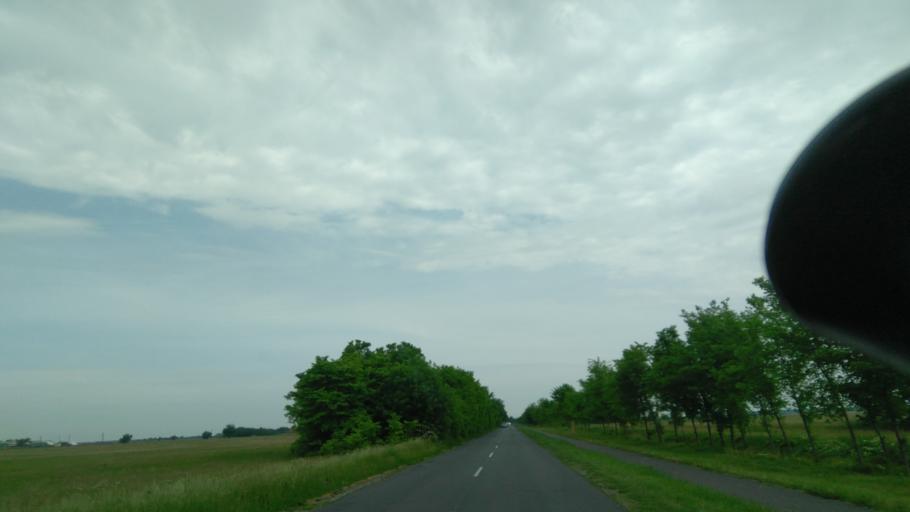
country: HU
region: Bekes
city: Szeghalom
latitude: 47.0411
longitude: 21.1853
